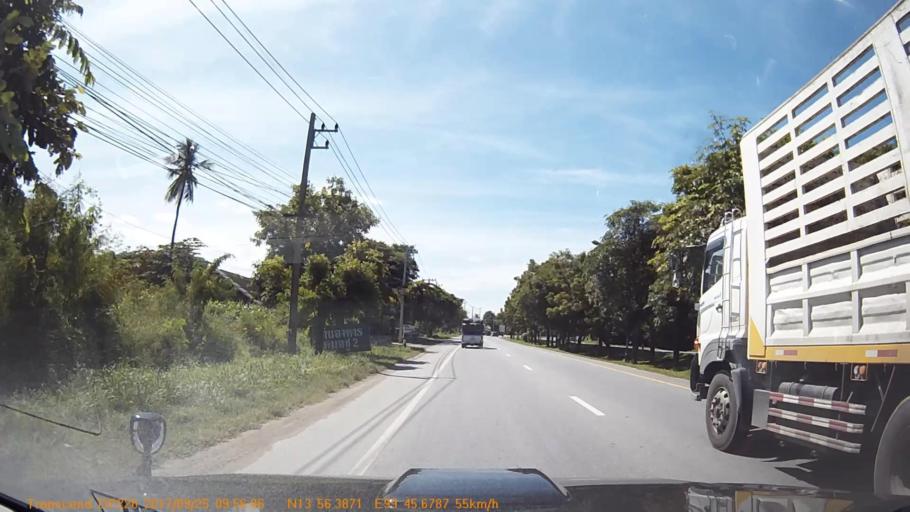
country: TH
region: Kanchanaburi
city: Tha Maka
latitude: 13.9395
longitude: 99.7614
